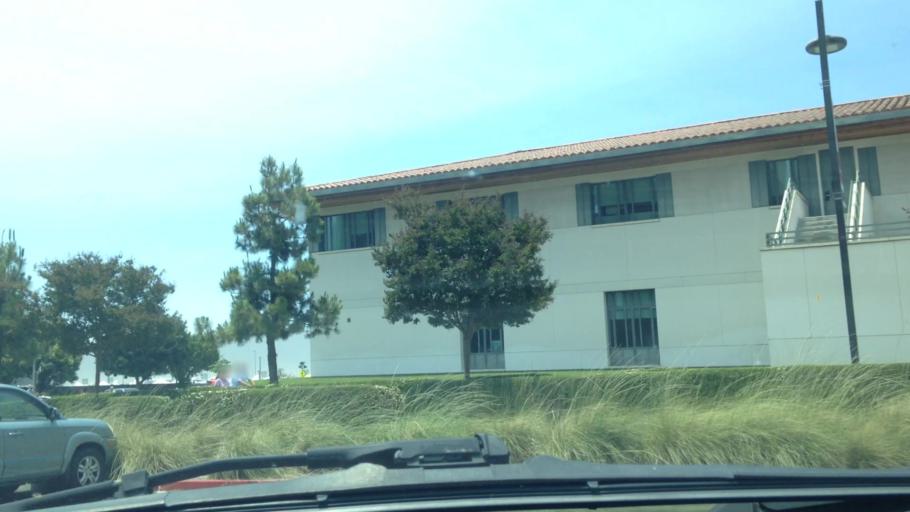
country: US
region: California
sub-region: Los Angeles County
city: Lakewood
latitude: 33.8306
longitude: -118.1357
